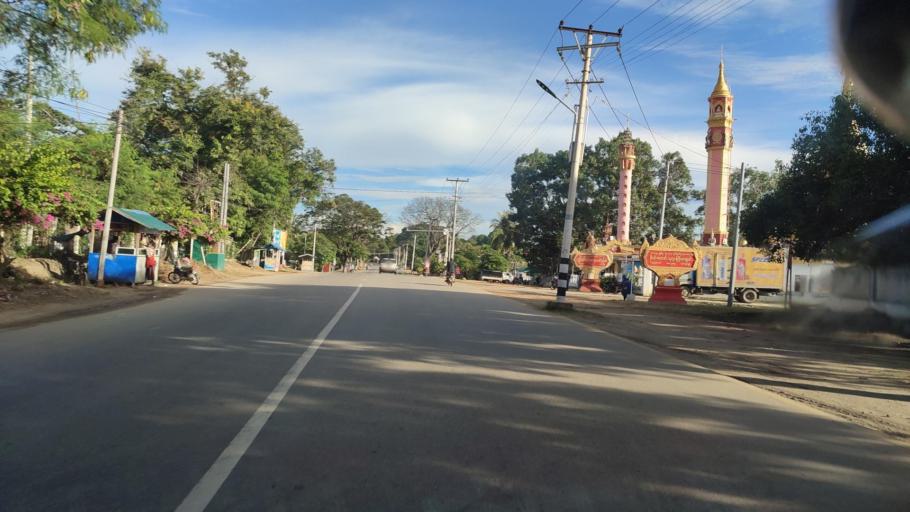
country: MM
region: Mandalay
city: Yamethin
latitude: 20.1393
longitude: 96.1966
